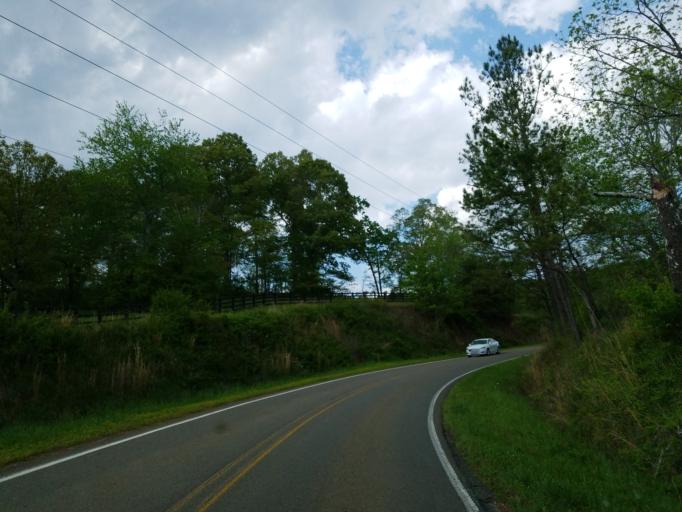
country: US
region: Georgia
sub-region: Pickens County
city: Jasper
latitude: 34.4381
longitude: -84.4528
